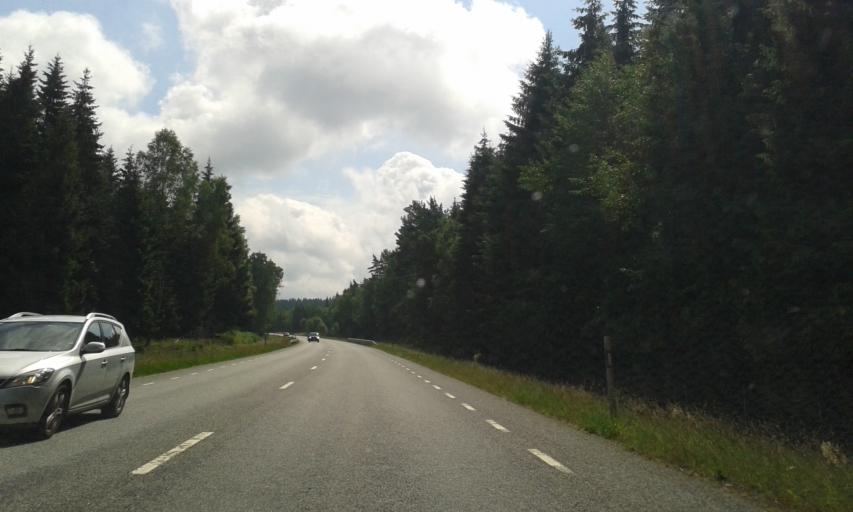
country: SE
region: Vaestra Goetaland
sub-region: Tranemo Kommun
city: Langhem
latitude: 57.5699
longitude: 13.2382
